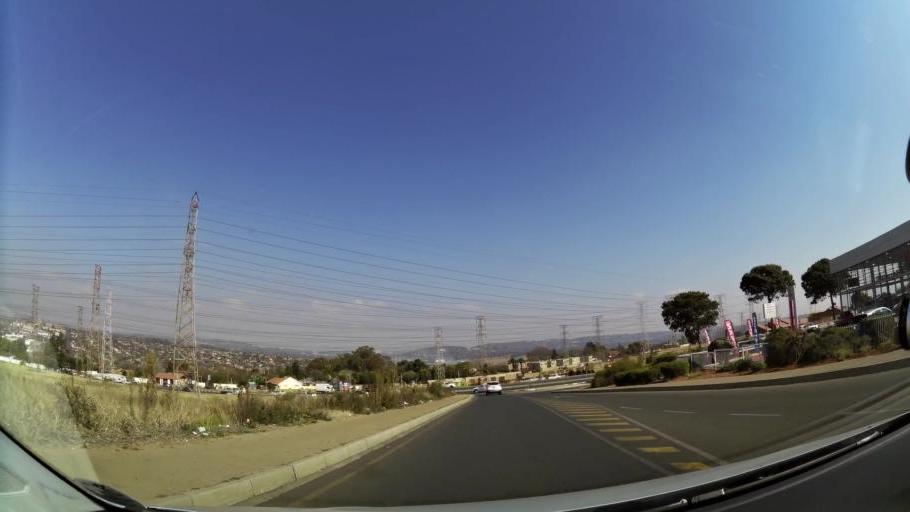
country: ZA
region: Gauteng
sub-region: City of Johannesburg Metropolitan Municipality
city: Modderfontein
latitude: -26.1239
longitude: 28.1418
